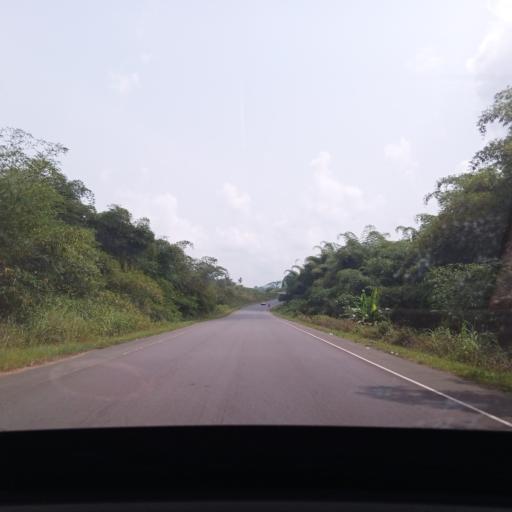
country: LR
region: Margibi
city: Kakata
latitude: 6.2535
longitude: -10.3083
